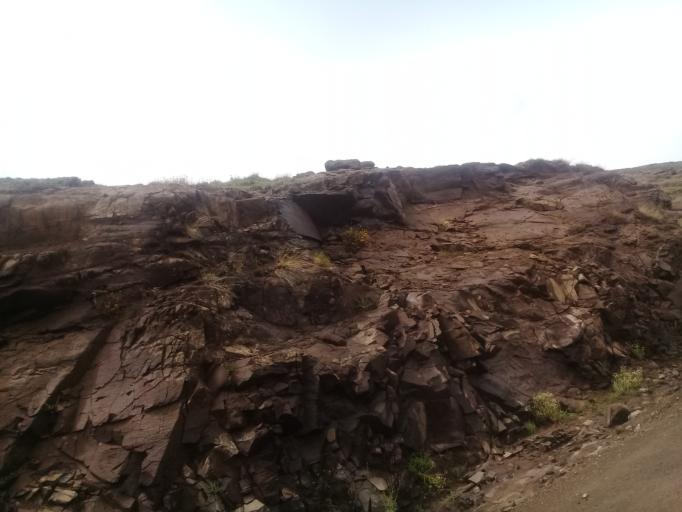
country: LS
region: Mokhotlong
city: Mokhotlong
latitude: -29.3363
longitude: 29.0296
